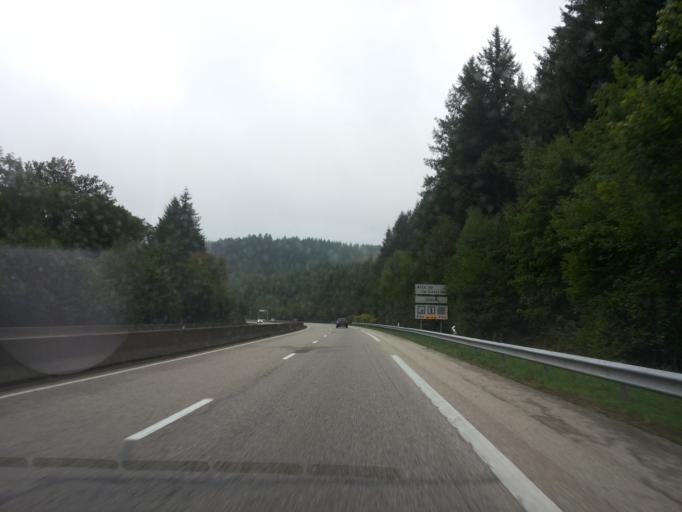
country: FR
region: Lorraine
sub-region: Departement des Vosges
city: Arches
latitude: 48.1463
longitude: 6.5059
